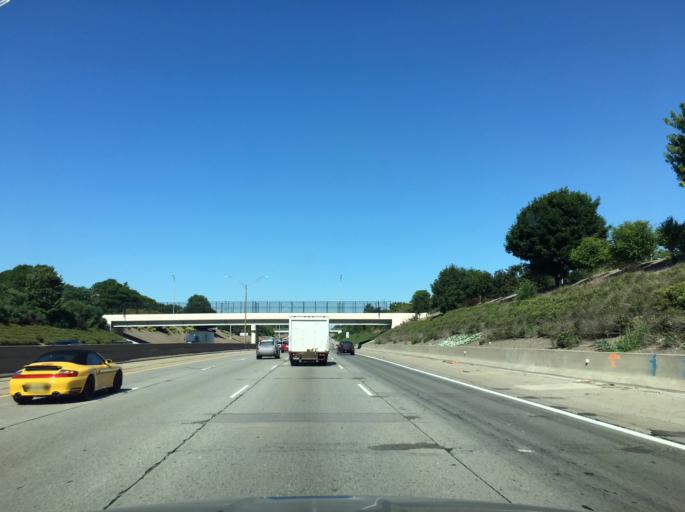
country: US
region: Michigan
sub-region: Macomb County
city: Eastpointe
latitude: 42.4927
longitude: -82.9874
